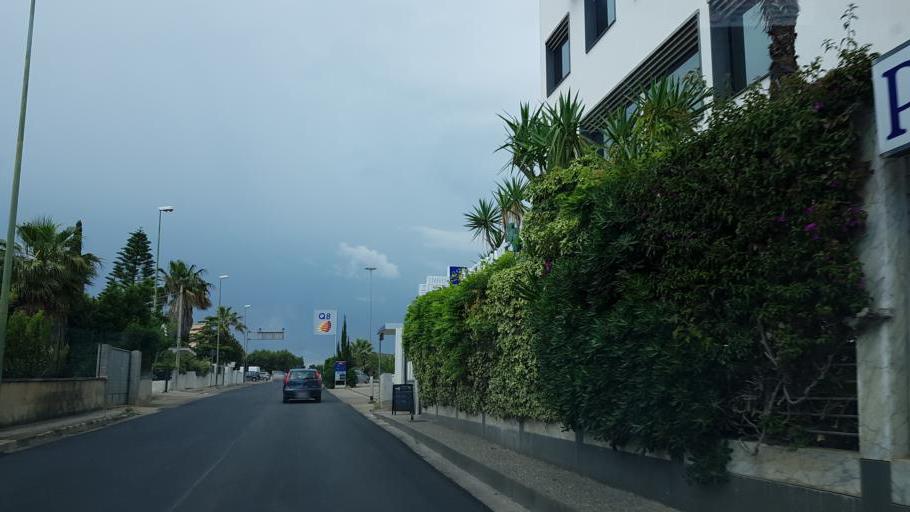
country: IT
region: Apulia
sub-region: Provincia di Lecce
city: Porto Cesareo
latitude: 40.2935
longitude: 17.8545
